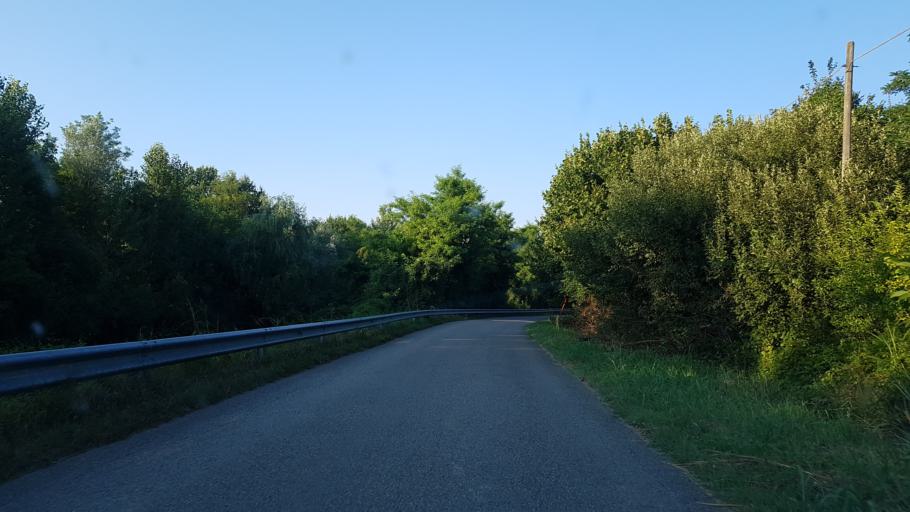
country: IT
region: Friuli Venezia Giulia
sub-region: Provincia di Gorizia
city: Capriva del Friuli
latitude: 45.9507
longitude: 13.5174
